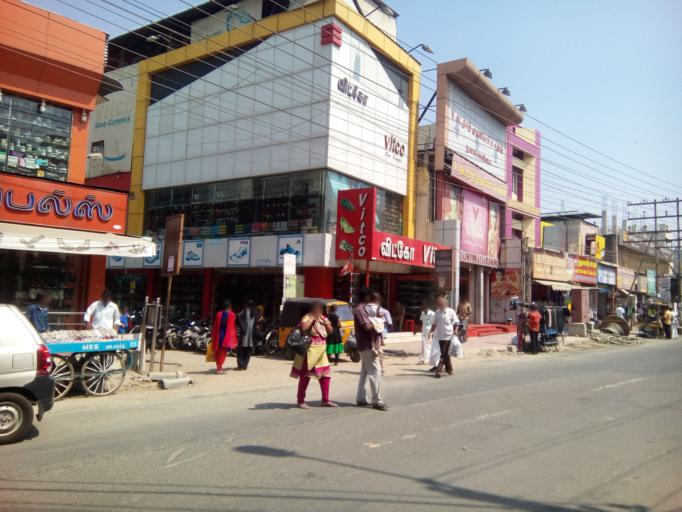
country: IN
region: Tamil Nadu
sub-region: Coimbatore
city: Coimbatore
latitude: 11.0171
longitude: 76.9668
